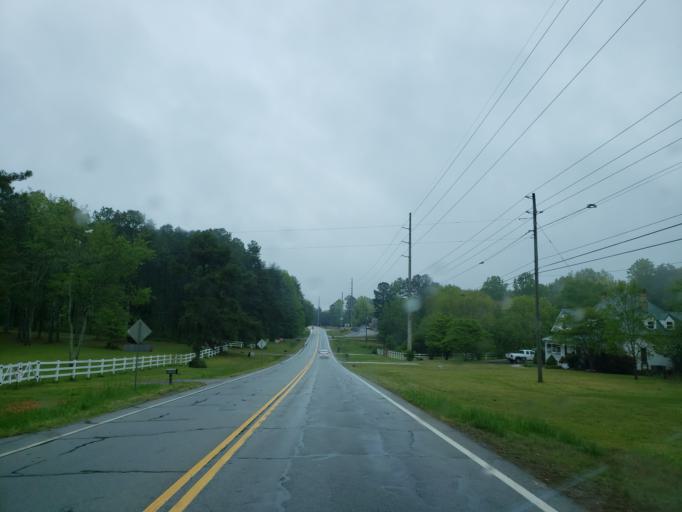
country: US
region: Georgia
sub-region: Paulding County
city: Dallas
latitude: 33.8608
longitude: -84.8433
